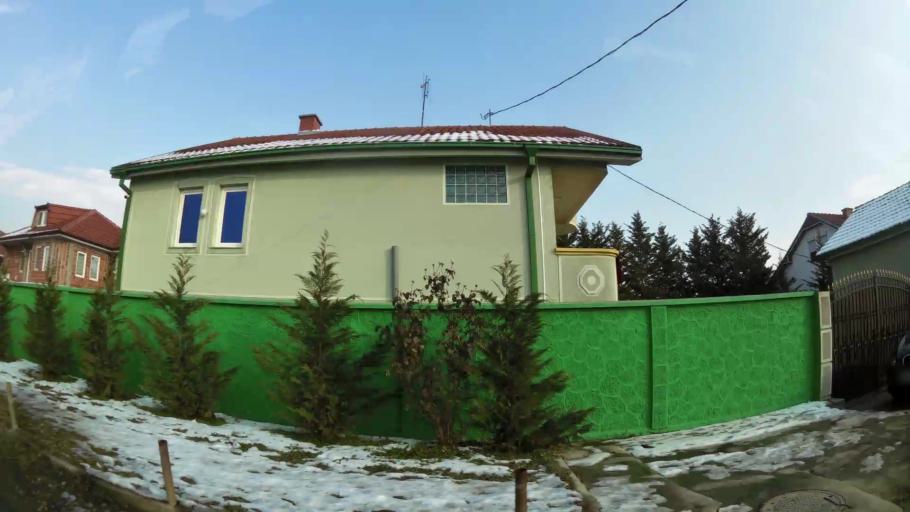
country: MK
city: Creshevo
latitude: 42.0215
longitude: 21.5094
